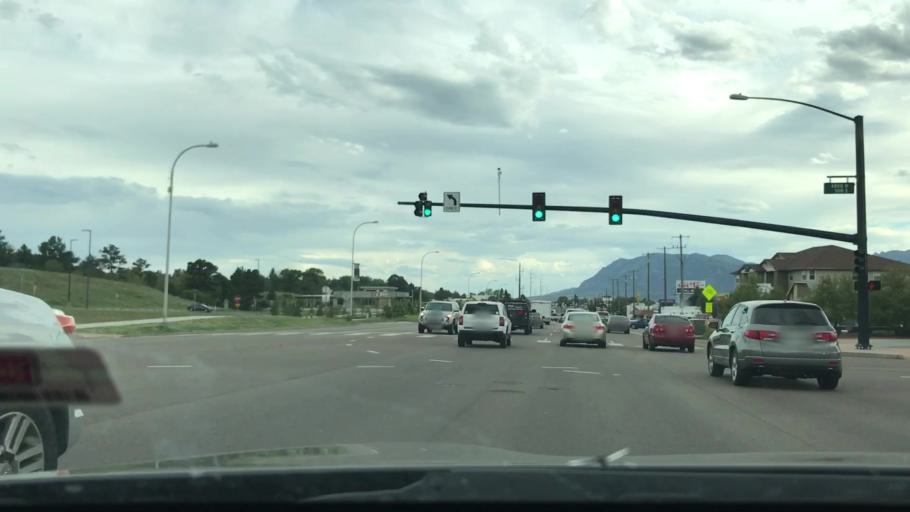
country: US
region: Colorado
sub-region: El Paso County
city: Colorado Springs
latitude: 38.9010
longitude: -104.8178
